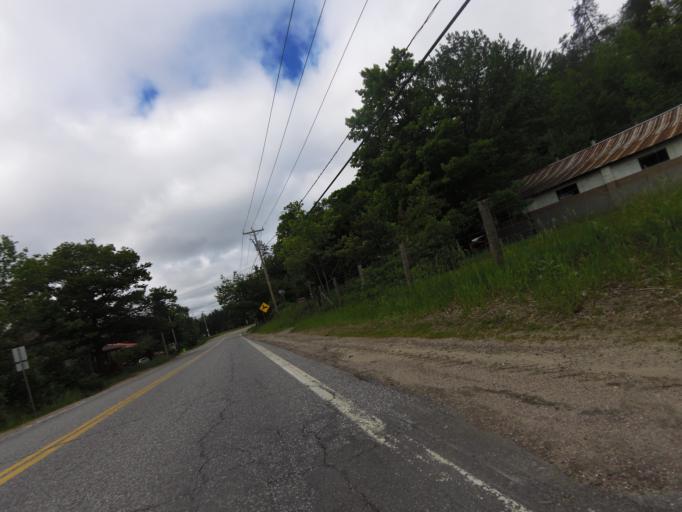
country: CA
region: Quebec
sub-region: Outaouais
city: Shawville
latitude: 45.8394
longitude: -76.4427
